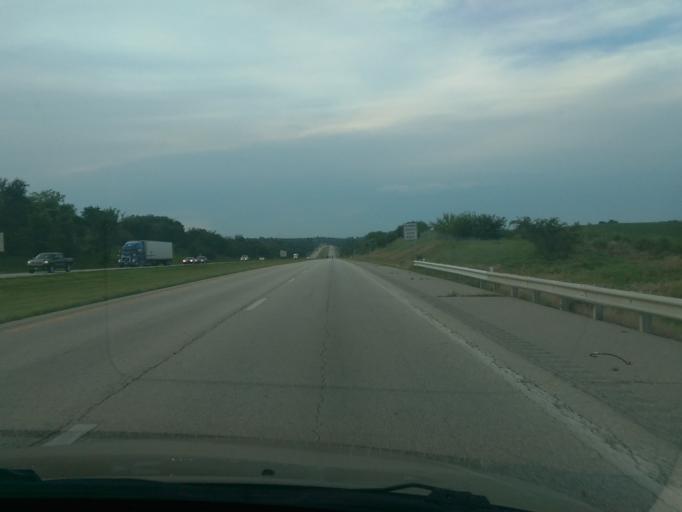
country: US
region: Missouri
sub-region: Andrew County
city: Country Club Village
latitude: 39.8299
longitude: -94.8052
